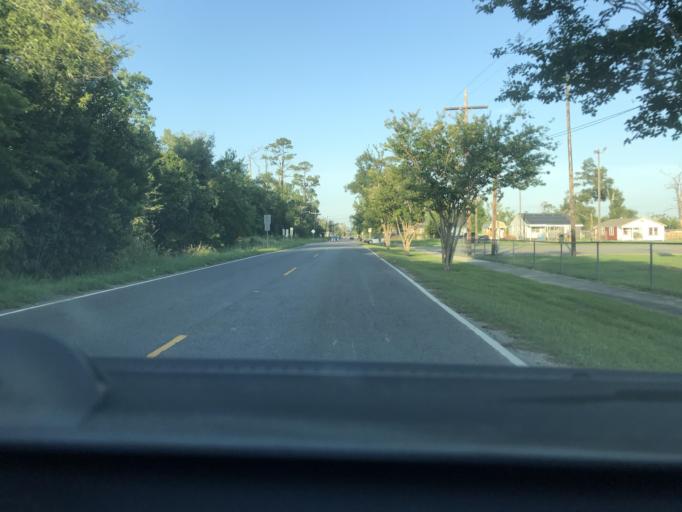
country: US
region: Louisiana
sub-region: Calcasieu Parish
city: Moss Bluff
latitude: 30.2641
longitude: -93.1879
